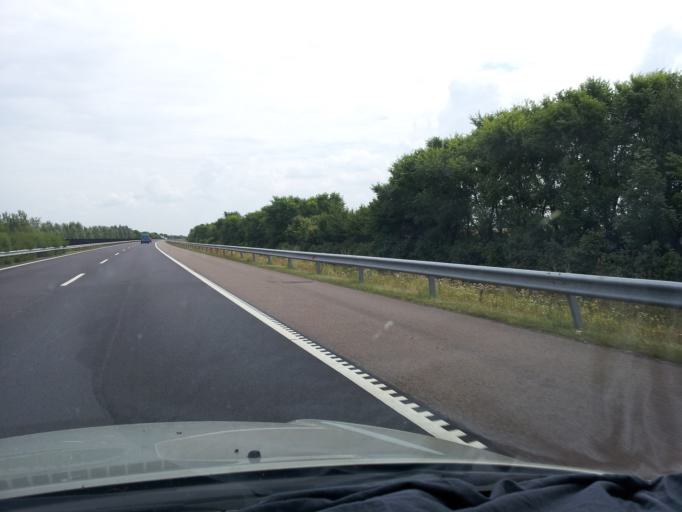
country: HU
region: Borsod-Abauj-Zemplen
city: Szentistvan
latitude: 47.7986
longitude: 20.6484
